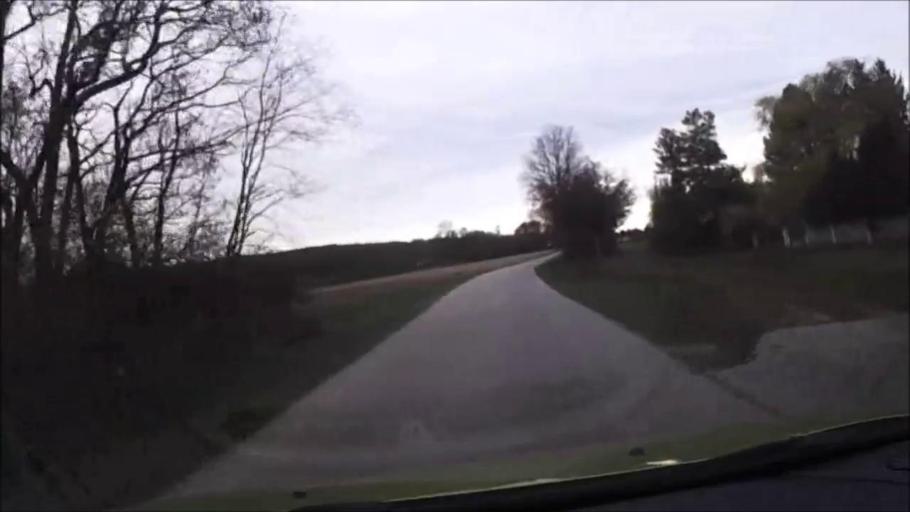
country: AT
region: Burgenland
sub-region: Eisenstadt-Umgebung
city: Loretto
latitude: 47.9095
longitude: 16.5147
